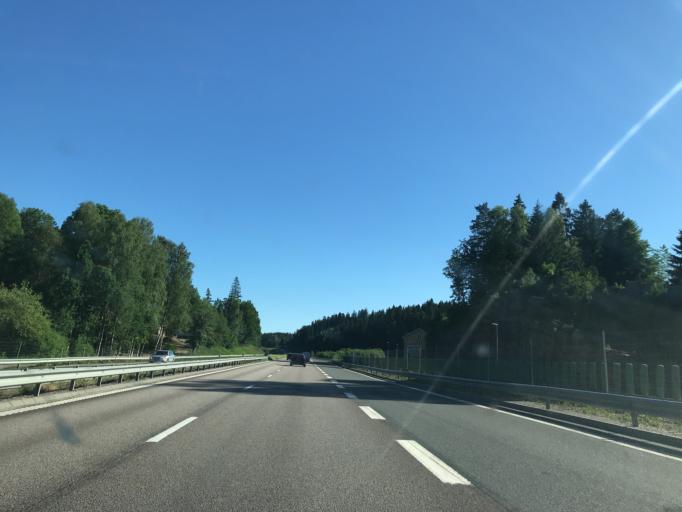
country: SE
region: Vaestra Goetaland
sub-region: Alingsas Kommun
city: Ingared
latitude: 57.8944
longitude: 12.4885
